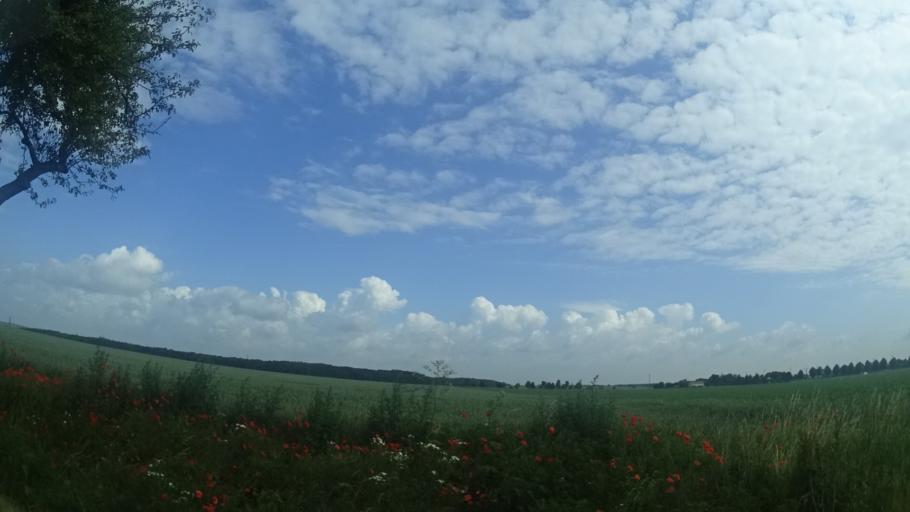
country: DE
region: Lower Saxony
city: Pattensen
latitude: 52.2094
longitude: 9.7397
